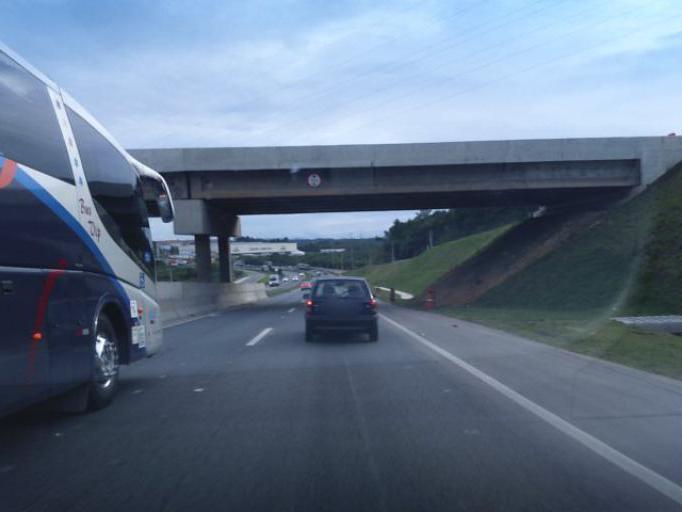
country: BR
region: Parana
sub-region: Sao Jose Dos Pinhais
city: Sao Jose dos Pinhais
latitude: -25.5937
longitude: -49.1728
